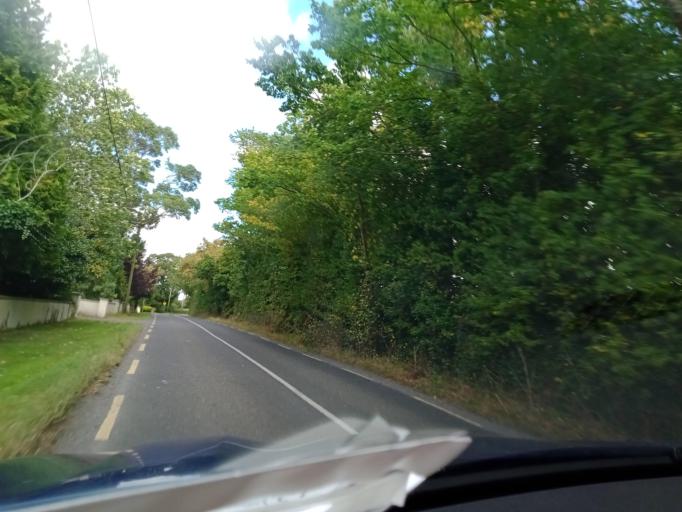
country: IE
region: Leinster
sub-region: Laois
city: Portlaoise
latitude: 53.0038
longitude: -7.2768
